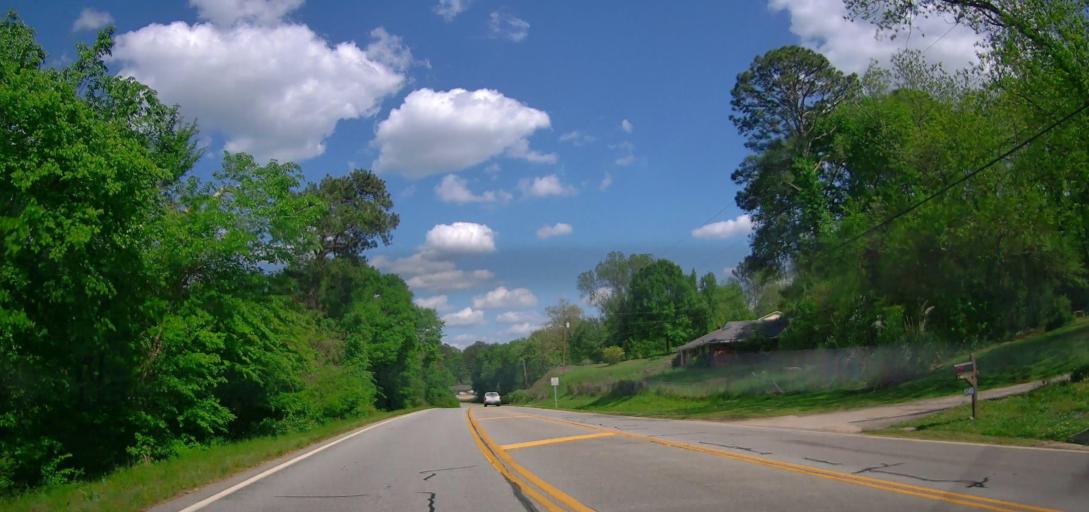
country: US
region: Georgia
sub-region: Greene County
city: Greensboro
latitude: 33.5762
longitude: -83.1940
